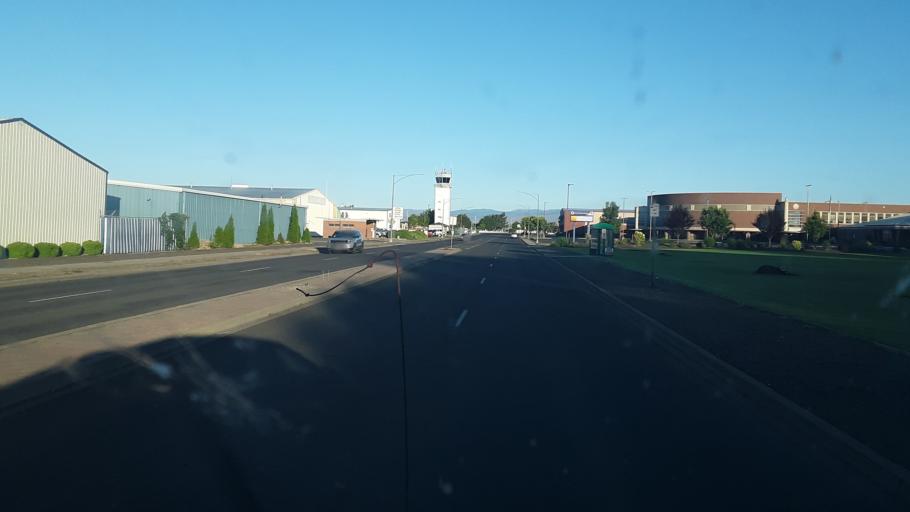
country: US
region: Washington
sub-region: Yakima County
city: Yakima
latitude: 46.5709
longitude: -120.5343
